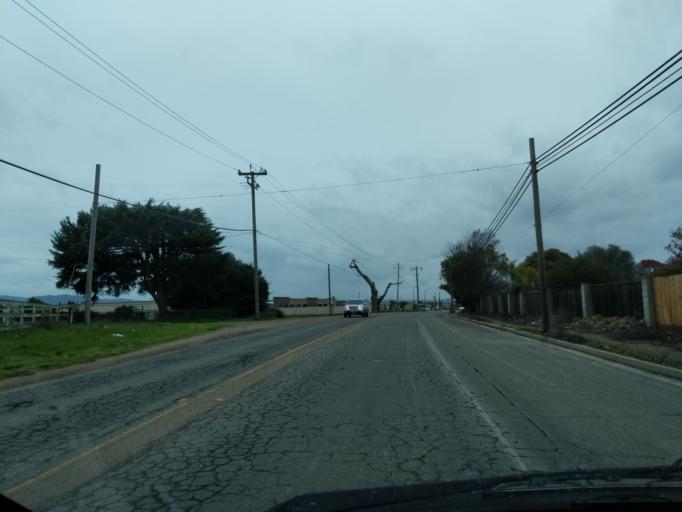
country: US
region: California
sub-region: Monterey County
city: Boronda
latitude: 36.7230
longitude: -121.6474
